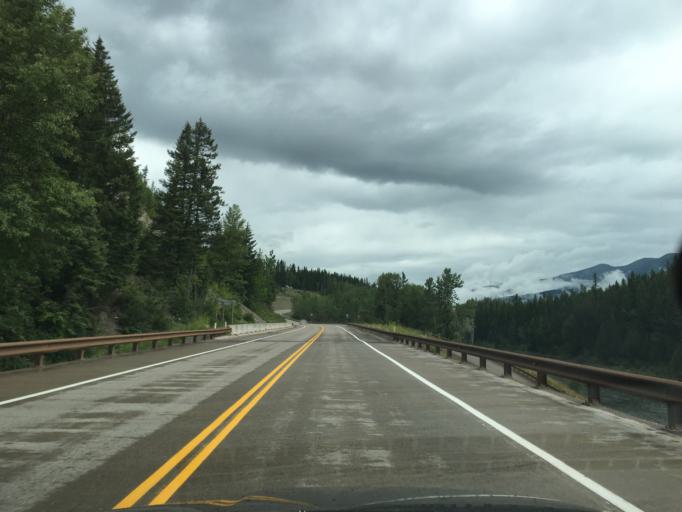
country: US
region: Montana
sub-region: Flathead County
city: Bigfork
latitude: 48.2754
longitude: -113.6047
